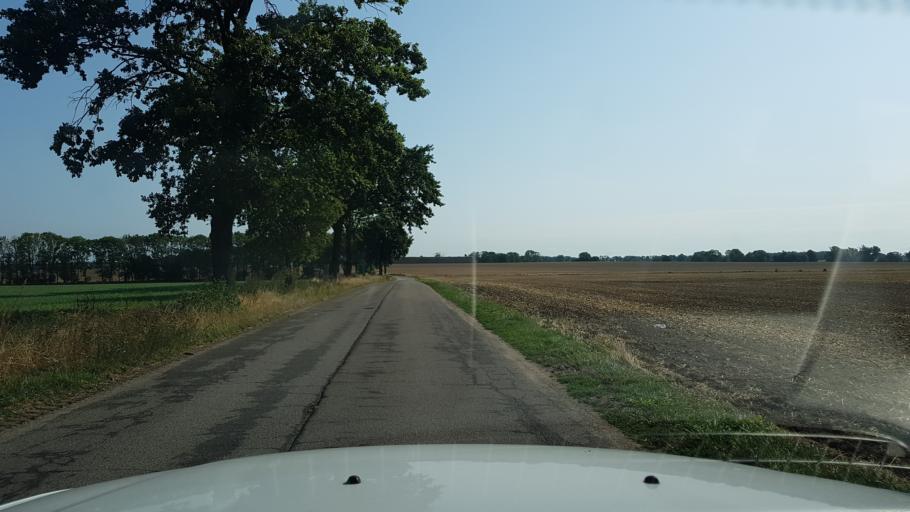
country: PL
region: West Pomeranian Voivodeship
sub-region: Powiat stargardzki
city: Stargard Szczecinski
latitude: 53.2621
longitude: 15.1096
